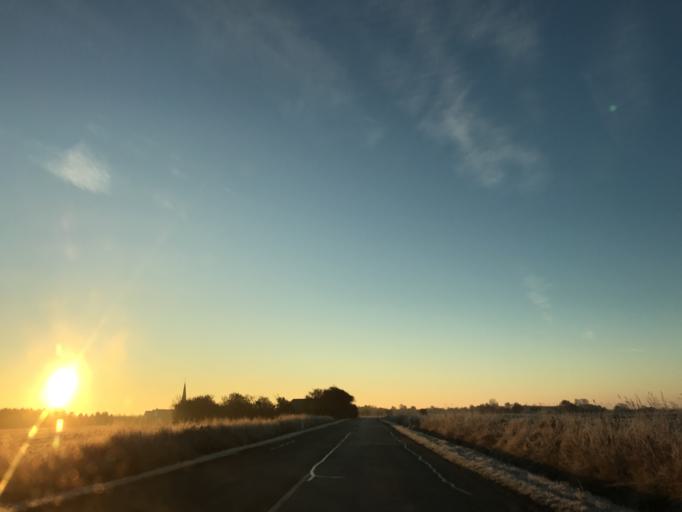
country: DK
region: South Denmark
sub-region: Haderslev Kommune
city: Starup
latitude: 55.2033
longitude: 9.5114
